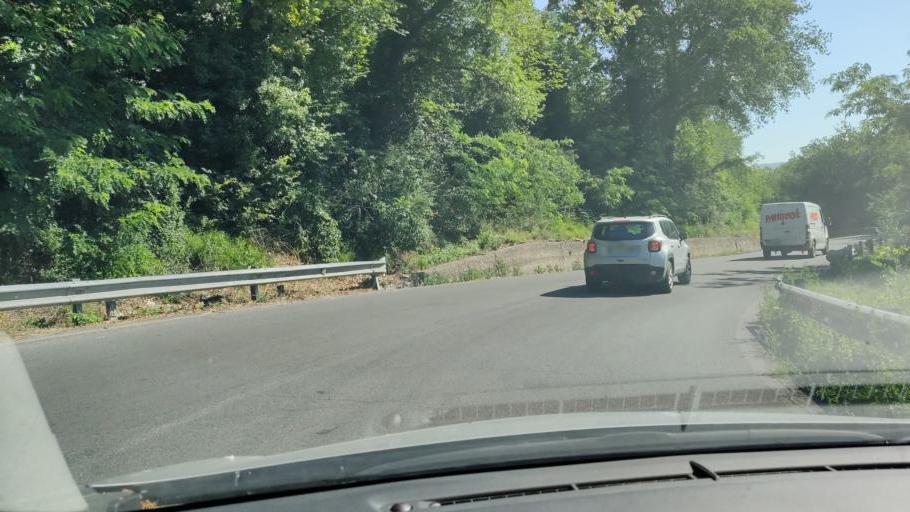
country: IT
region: Umbria
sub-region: Provincia di Perugia
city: Todi
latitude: 42.7845
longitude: 12.4145
